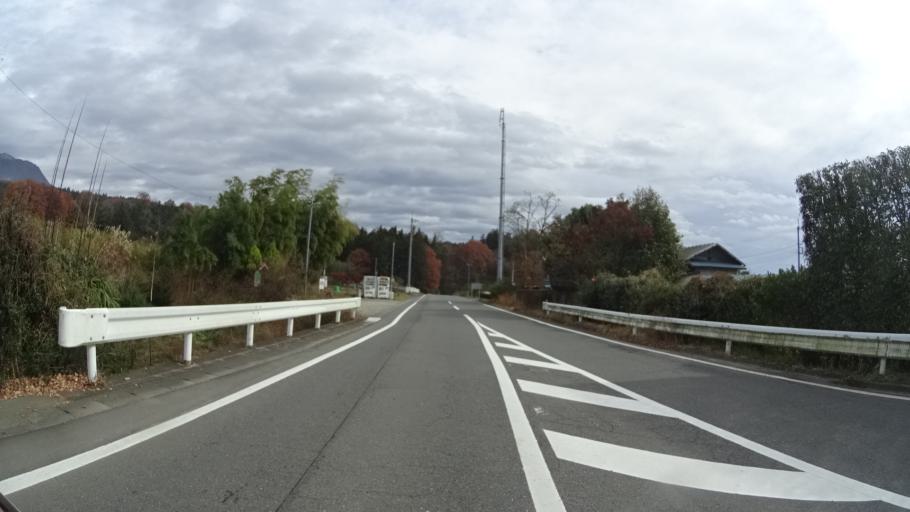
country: JP
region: Gunma
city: Maebashi-shi
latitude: 36.4810
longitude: 139.1141
